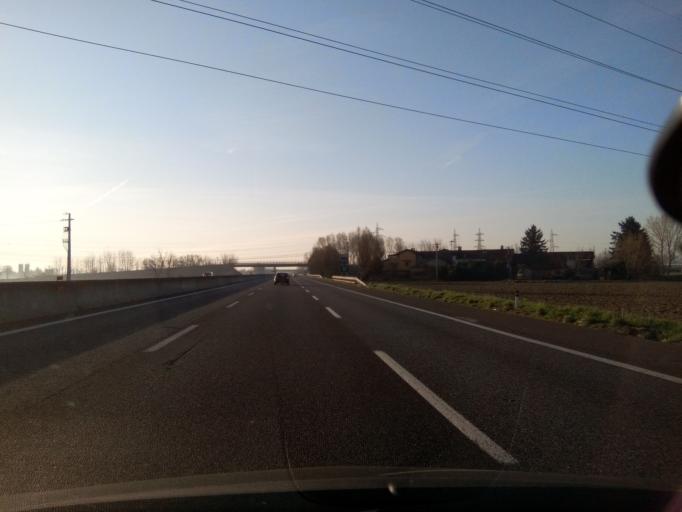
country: IT
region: Lombardy
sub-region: Provincia di Lodi
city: San Rocco al Porto
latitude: 45.0988
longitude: 9.6996
